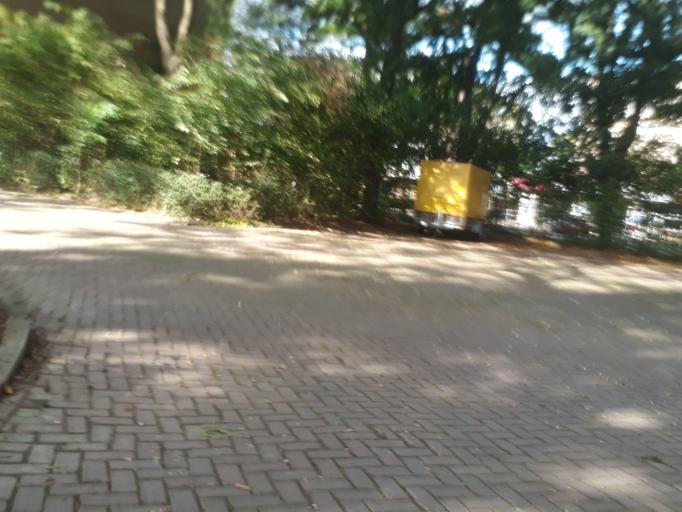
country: NL
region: Gelderland
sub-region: Gemeente Zevenaar
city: Zevenaar
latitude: 51.9297
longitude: 6.0629
